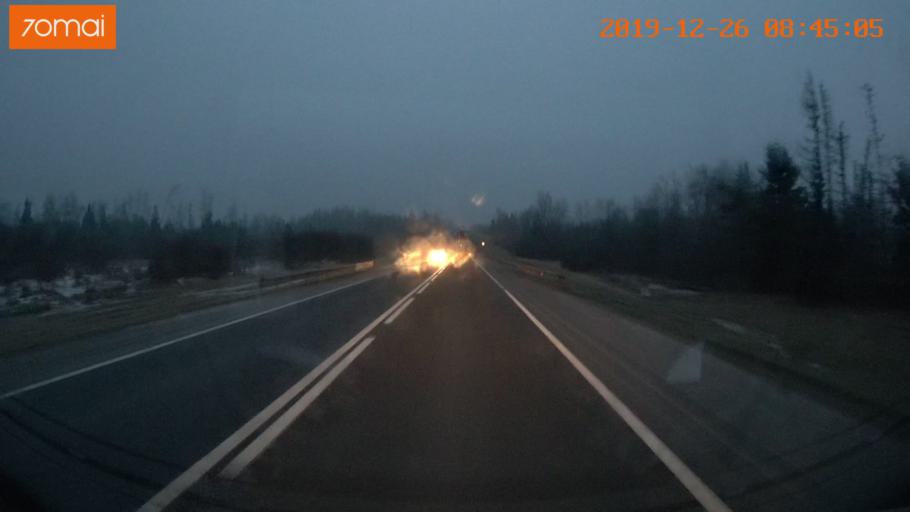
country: RU
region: Jaroslavl
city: Prechistoye
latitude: 58.5945
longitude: 40.3441
